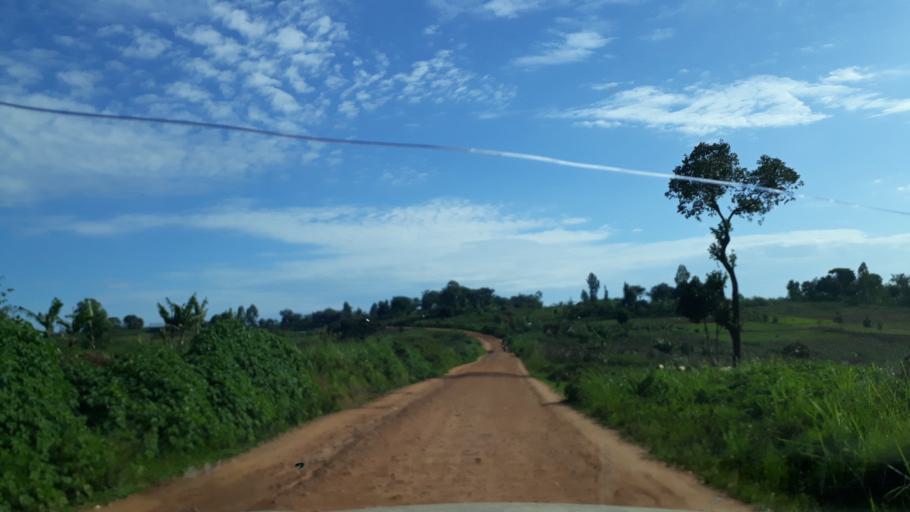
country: UG
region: Northern Region
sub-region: Zombo District
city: Paidha
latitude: 2.3230
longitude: 31.0250
